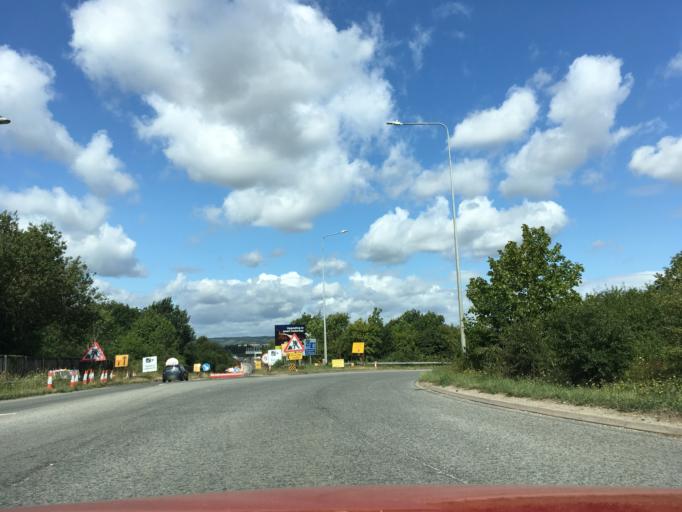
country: GB
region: England
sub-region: Kent
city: Aylesford
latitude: 51.2954
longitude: 0.4841
